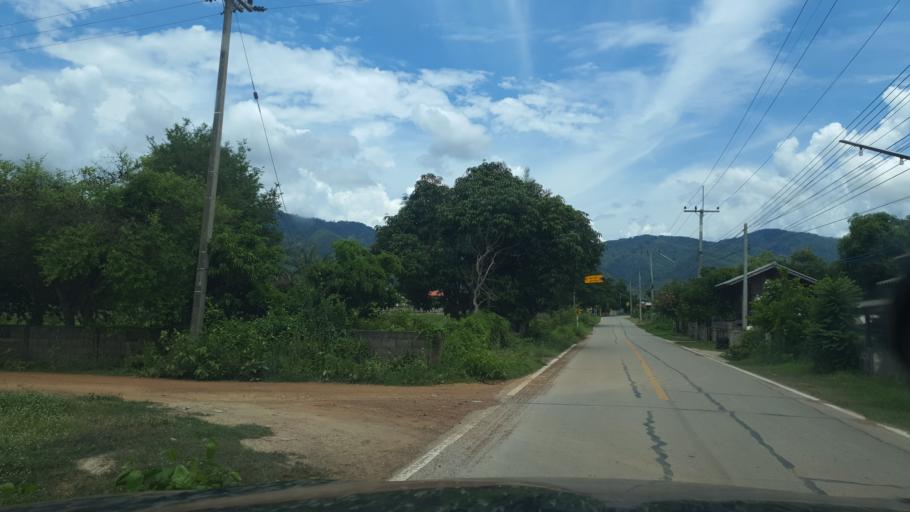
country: TH
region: Lampang
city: Sop Prap
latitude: 17.9108
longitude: 99.4132
